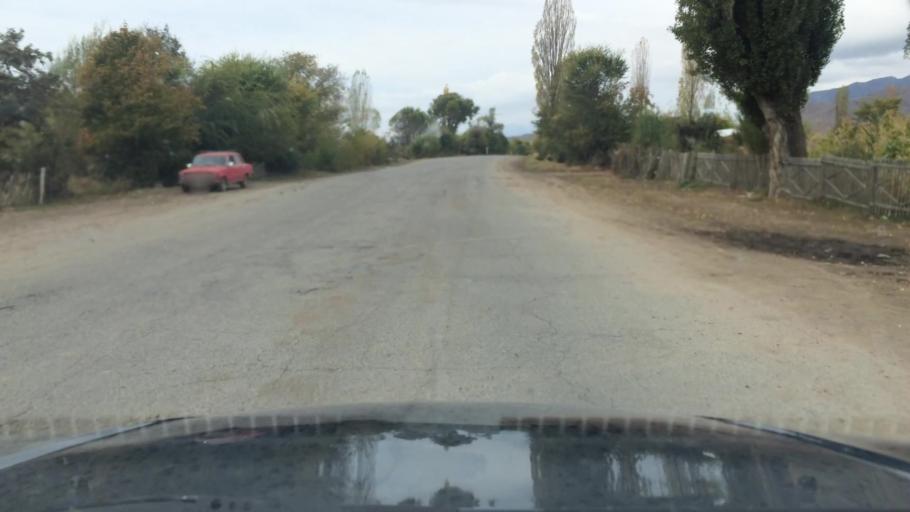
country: KG
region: Ysyk-Koel
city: Pokrovka
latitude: 42.7370
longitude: 77.9334
